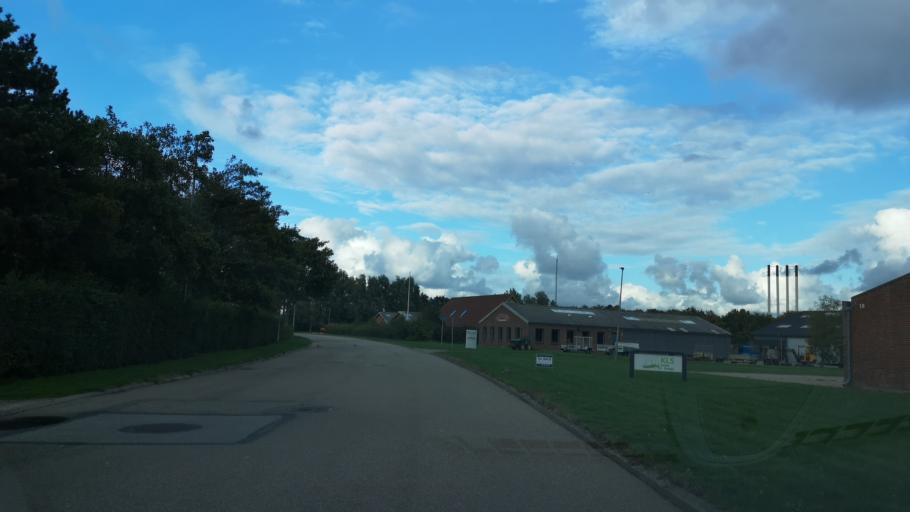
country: DK
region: Central Jutland
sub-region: Ringkobing-Skjern Kommune
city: Ringkobing
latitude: 56.0898
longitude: 8.2700
